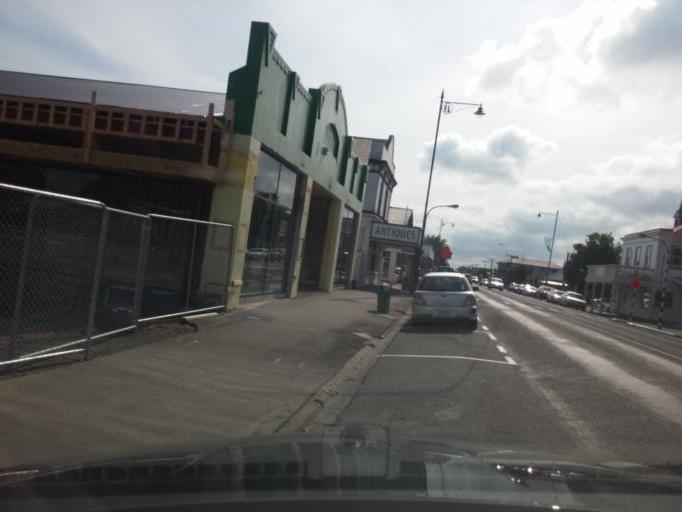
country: NZ
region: Wellington
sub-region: Masterton District
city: Masterton
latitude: -41.0793
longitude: 175.4615
